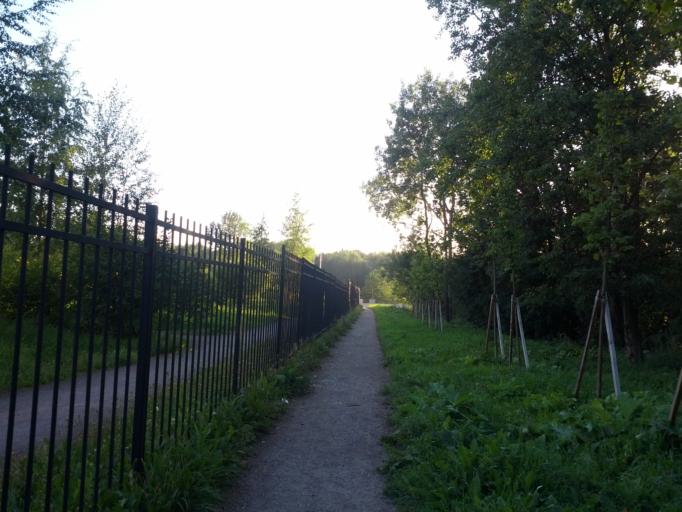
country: RU
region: St.-Petersburg
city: Krasnogvargeisky
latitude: 59.9116
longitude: 30.4906
